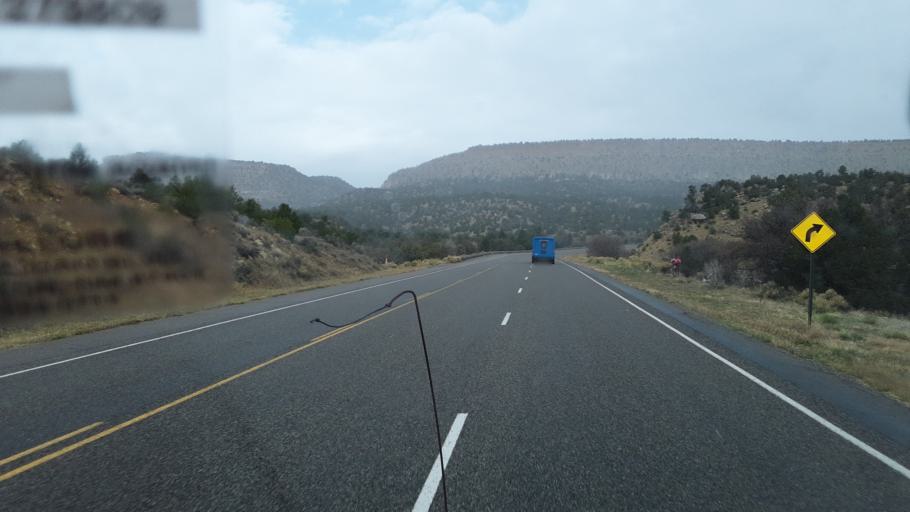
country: US
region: New Mexico
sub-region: Rio Arriba County
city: Santa Teresa
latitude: 36.3960
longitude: -106.4927
